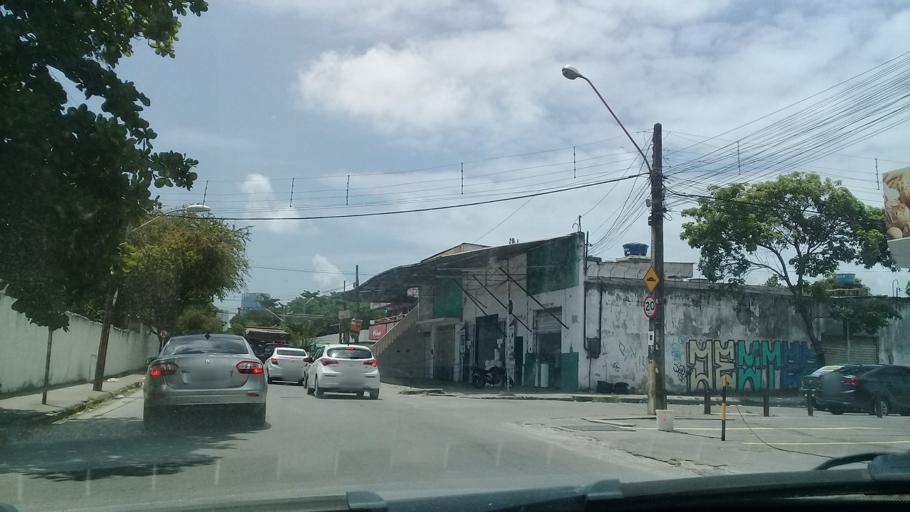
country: BR
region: Pernambuco
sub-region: Recife
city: Recife
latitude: -8.1079
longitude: -34.9173
